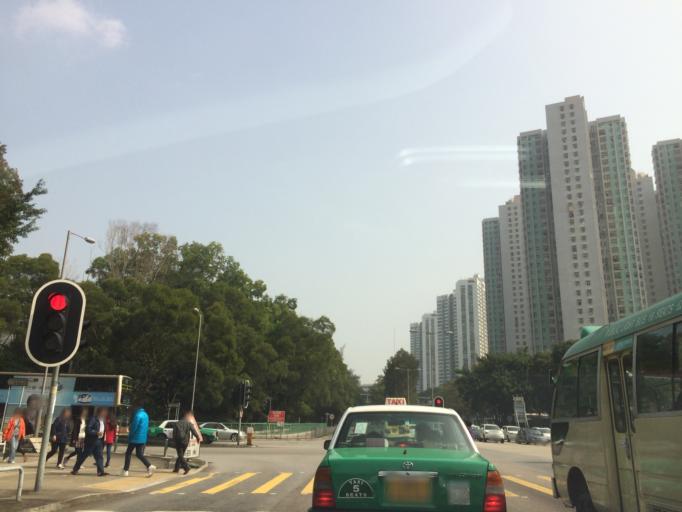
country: HK
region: Tai Po
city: Tai Po
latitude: 22.4561
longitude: 114.1716
